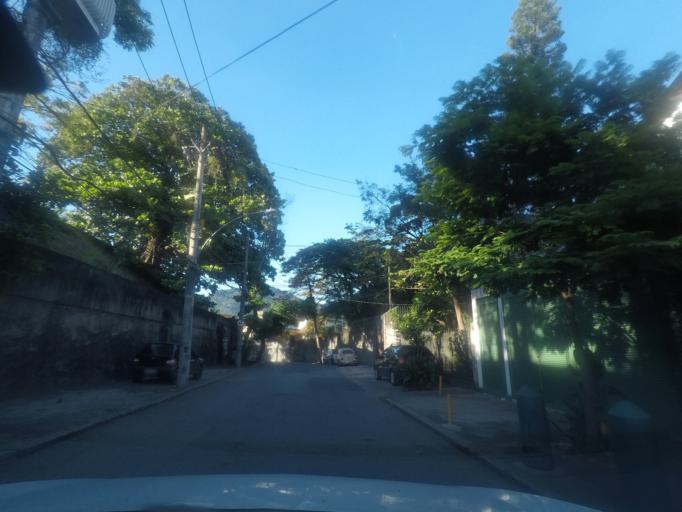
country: BR
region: Rio de Janeiro
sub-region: Rio De Janeiro
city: Rio de Janeiro
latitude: -22.9298
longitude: -43.1965
